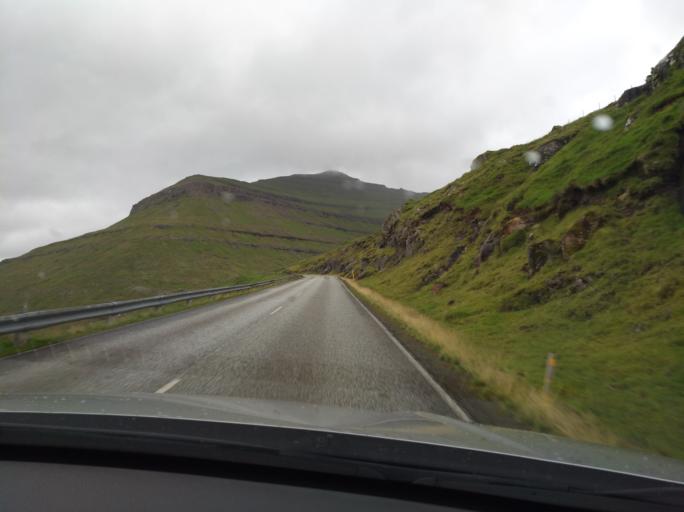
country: FO
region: Eysturoy
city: Fuglafjordur
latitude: 62.2204
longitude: -6.8709
